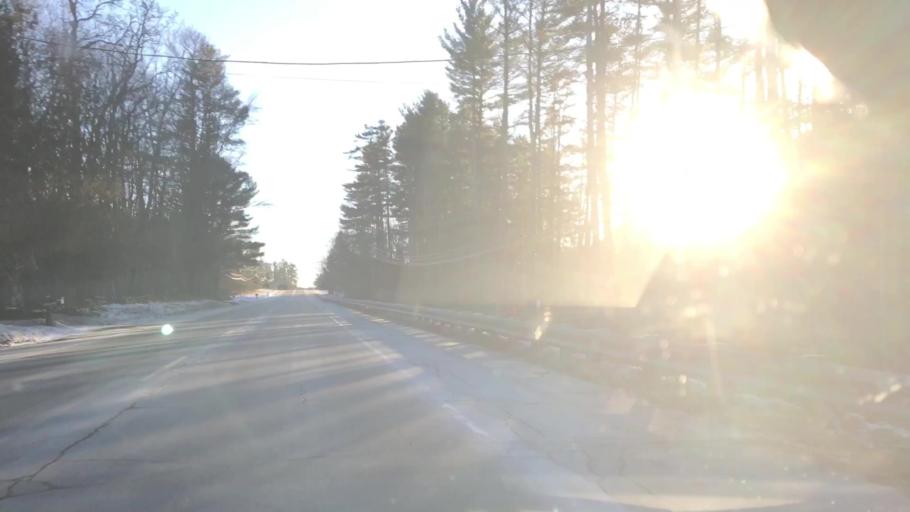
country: US
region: New Hampshire
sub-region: Grafton County
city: Lyme
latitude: 43.7996
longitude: -72.1679
